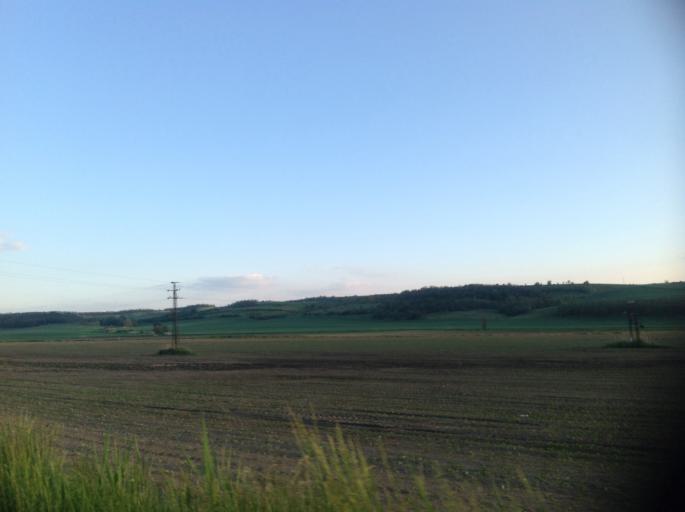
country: HU
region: Komarom-Esztergom
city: Sarisap
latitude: 47.6614
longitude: 18.6994
